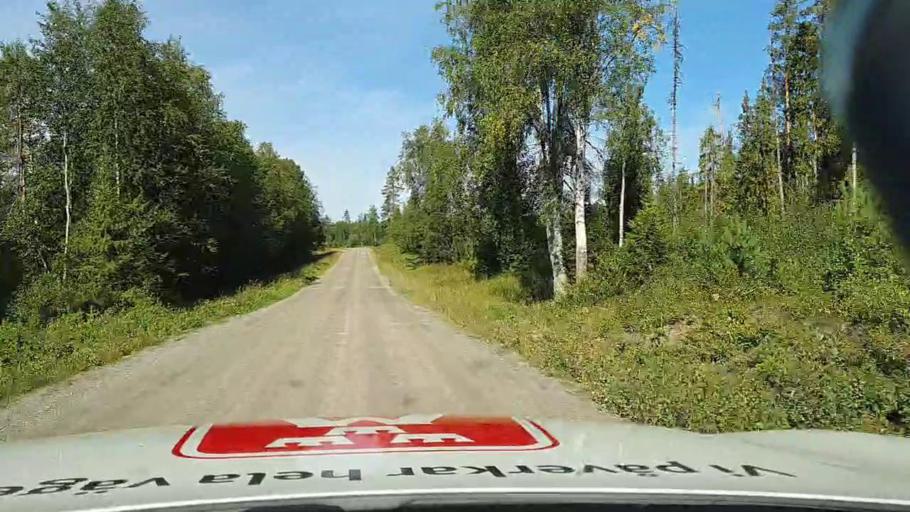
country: SE
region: Jaemtland
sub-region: Stroemsunds Kommun
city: Stroemsund
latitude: 63.7141
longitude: 15.3001
